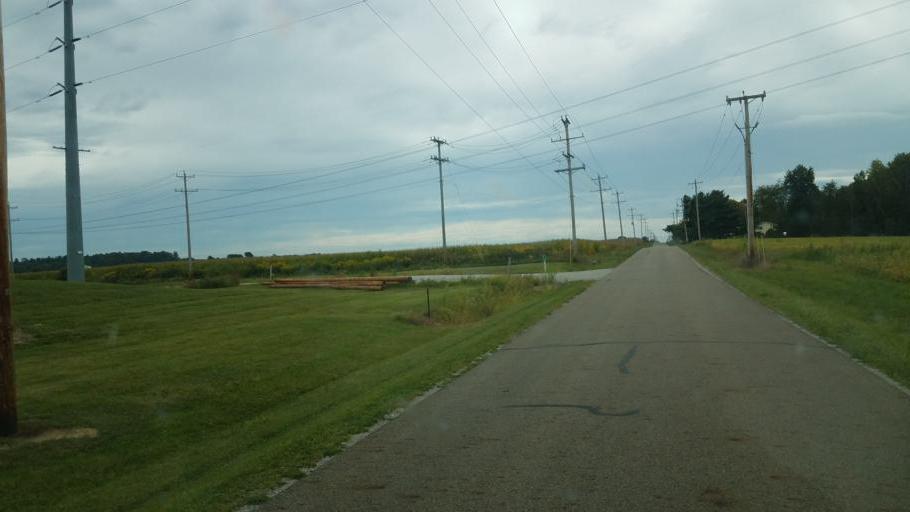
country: US
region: Ohio
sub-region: Knox County
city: Centerburg
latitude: 40.2677
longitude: -82.7197
